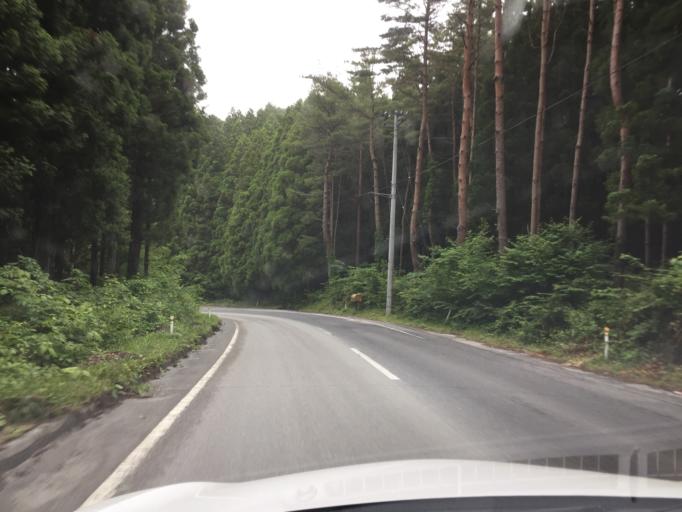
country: JP
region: Fukushima
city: Funehikimachi-funehiki
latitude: 37.3114
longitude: 140.7100
